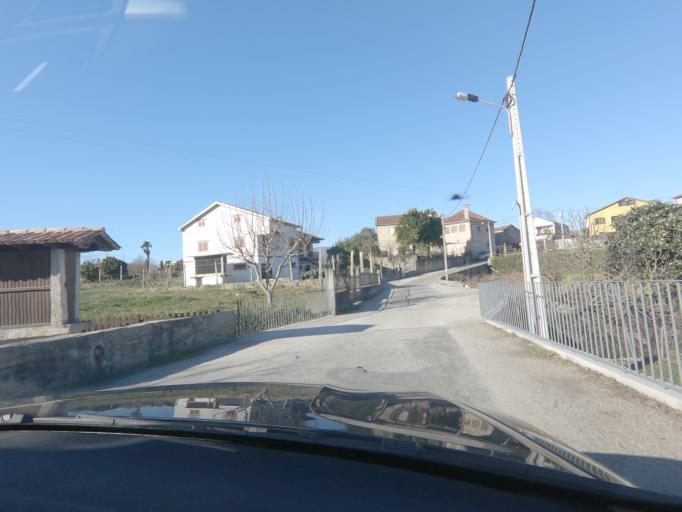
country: PT
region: Viseu
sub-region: Oliveira de Frades
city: Oliveira de Frades
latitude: 40.7340
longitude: -8.1583
